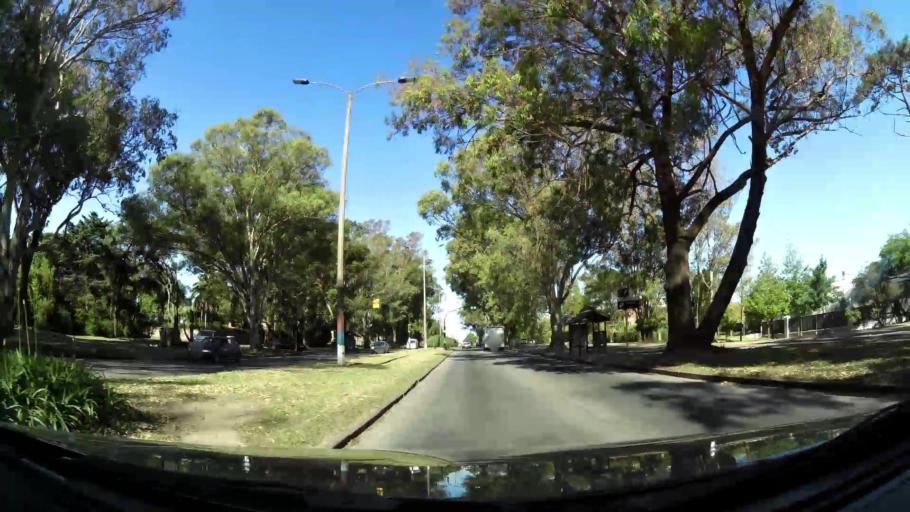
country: UY
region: Canelones
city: Paso de Carrasco
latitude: -34.8764
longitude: -56.0481
